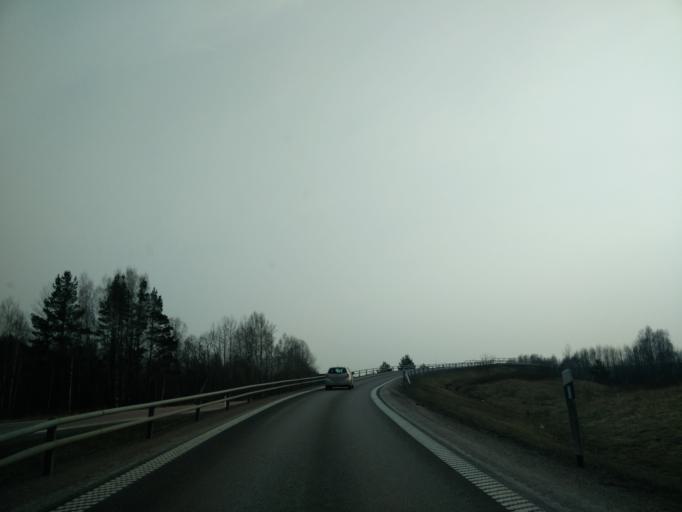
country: SE
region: Vaermland
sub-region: Karlstads Kommun
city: Karlstad
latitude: 59.4285
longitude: 13.4105
